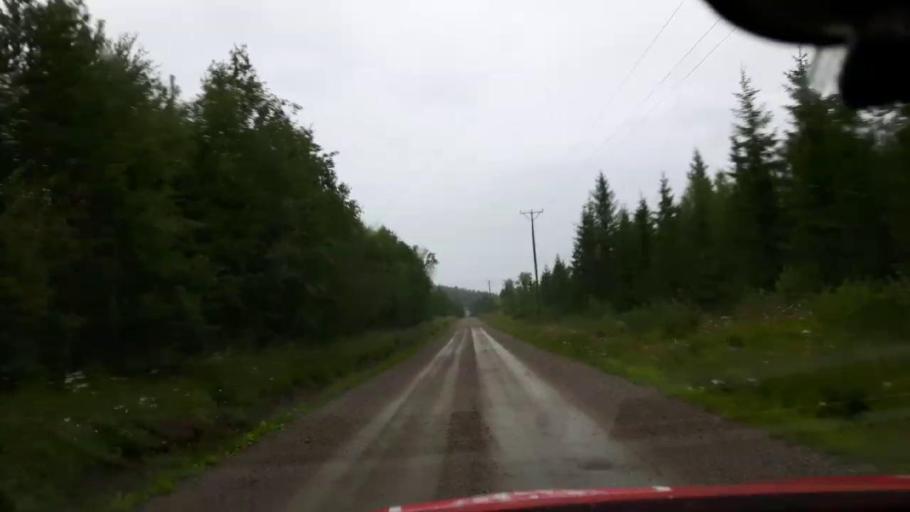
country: SE
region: Jaemtland
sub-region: OEstersunds Kommun
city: Brunflo
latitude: 62.7785
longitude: 14.9817
